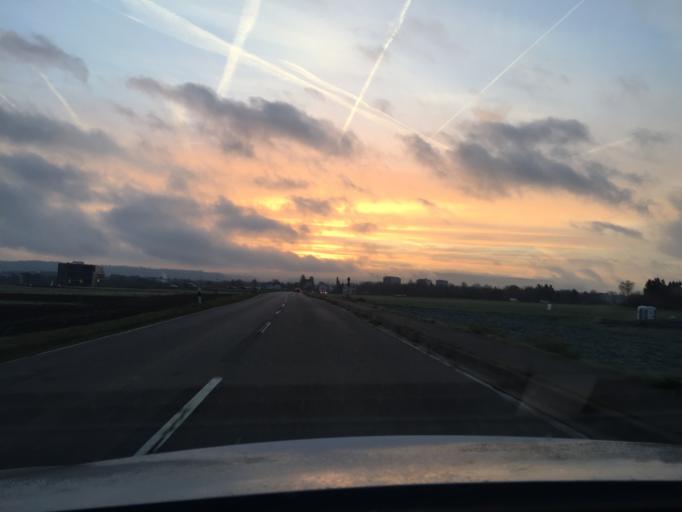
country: DE
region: Rheinland-Pfalz
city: Koblenz
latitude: 50.3775
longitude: 7.5586
